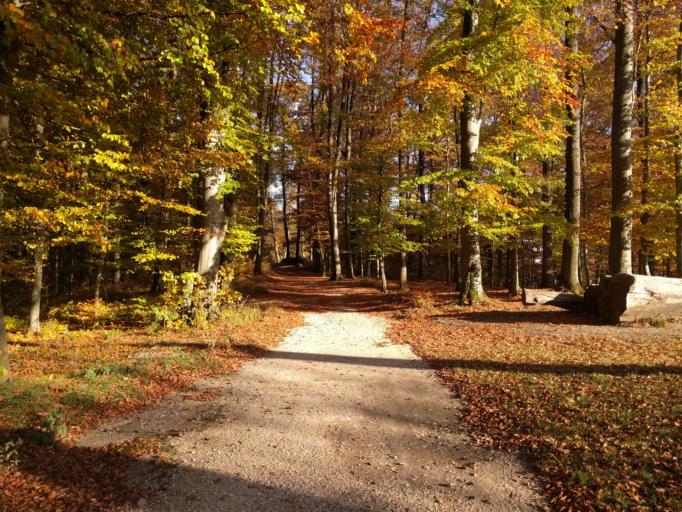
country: CH
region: Bern
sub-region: Biel/Bienne District
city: Brugg
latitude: 47.1391
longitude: 7.2663
